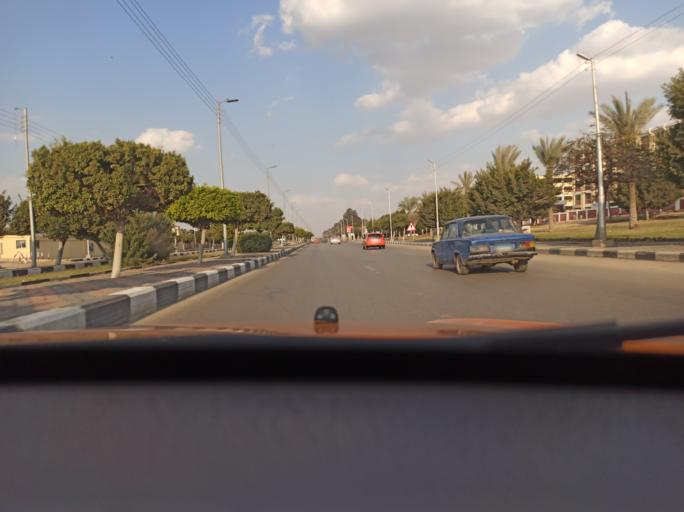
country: EG
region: Al Isma'iliyah
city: Ismailia
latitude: 30.6154
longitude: 32.2544
